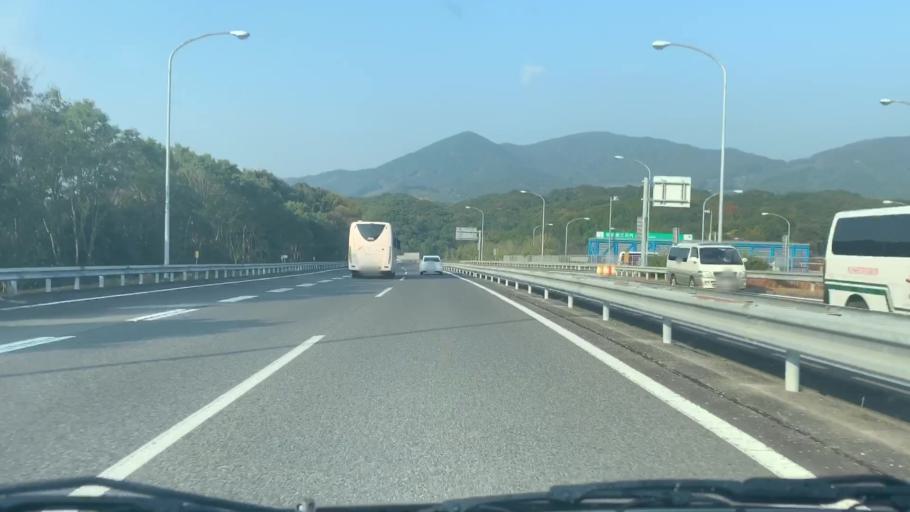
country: JP
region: Saga Prefecture
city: Imaricho-ko
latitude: 33.1699
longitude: 129.8462
